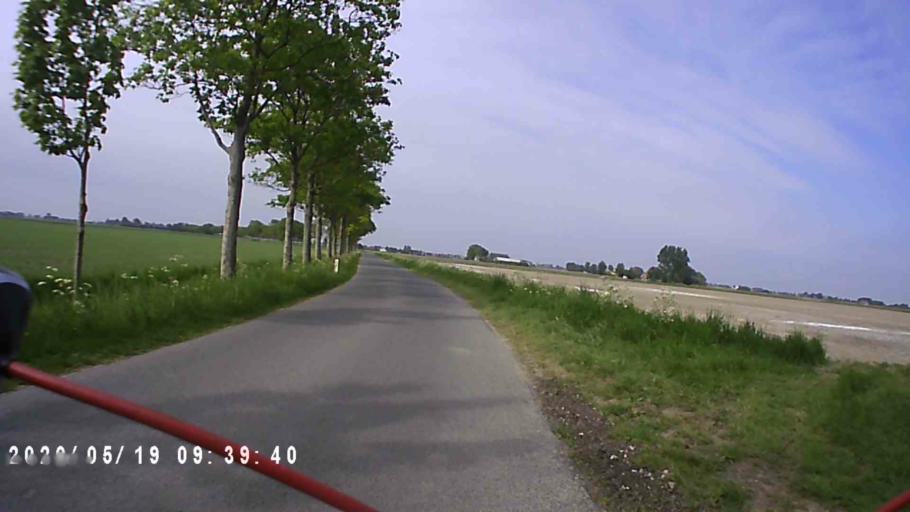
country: NL
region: Groningen
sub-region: Gemeente Zuidhorn
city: Grijpskerk
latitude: 53.2879
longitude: 6.2787
